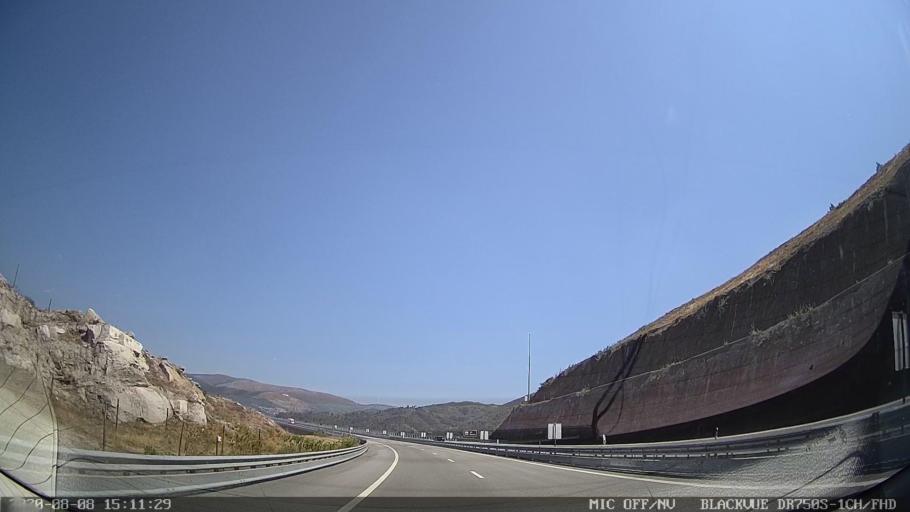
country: PT
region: Porto
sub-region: Amarante
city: Amarante
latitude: 41.2506
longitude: -7.9923
